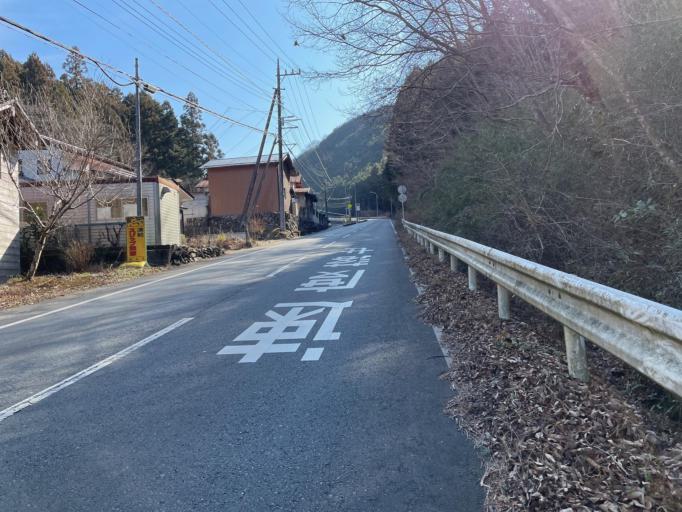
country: JP
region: Tokyo
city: Ome
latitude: 35.8606
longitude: 139.2386
